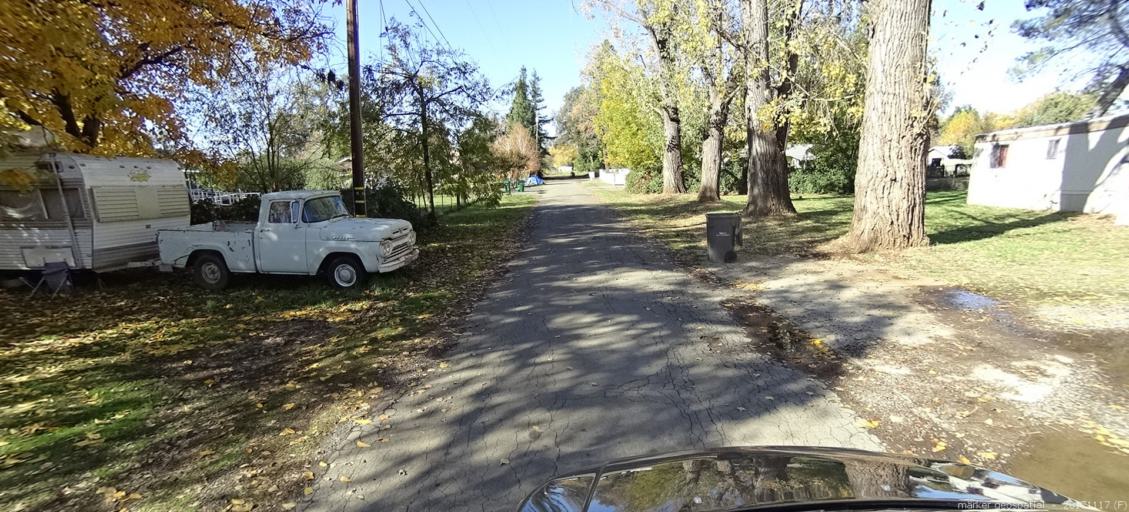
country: US
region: California
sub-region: Shasta County
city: Anderson
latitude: 40.4509
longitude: -122.2426
